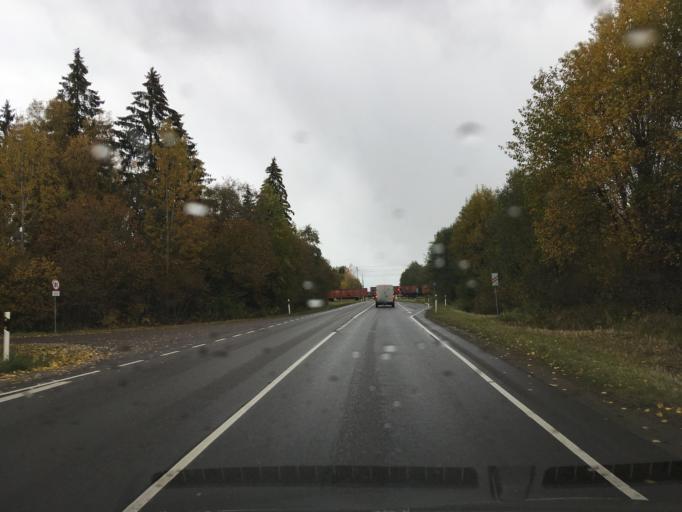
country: EE
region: Harju
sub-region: Anija vald
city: Kehra
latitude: 59.3424
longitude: 25.3104
